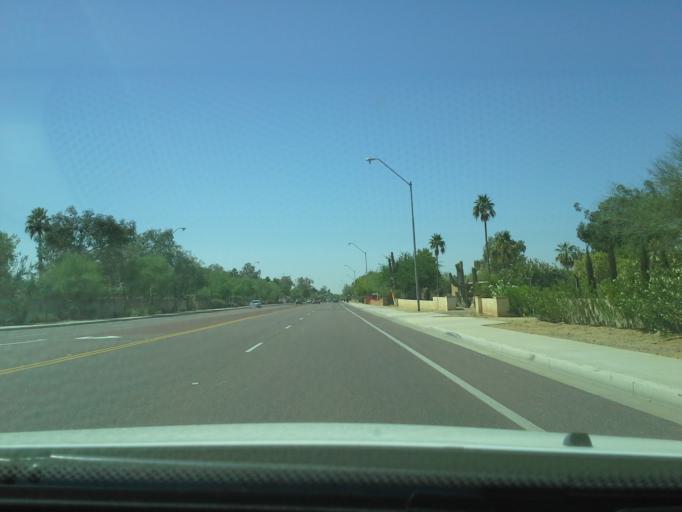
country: US
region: Arizona
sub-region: Maricopa County
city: Paradise Valley
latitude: 33.6109
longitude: -111.9086
